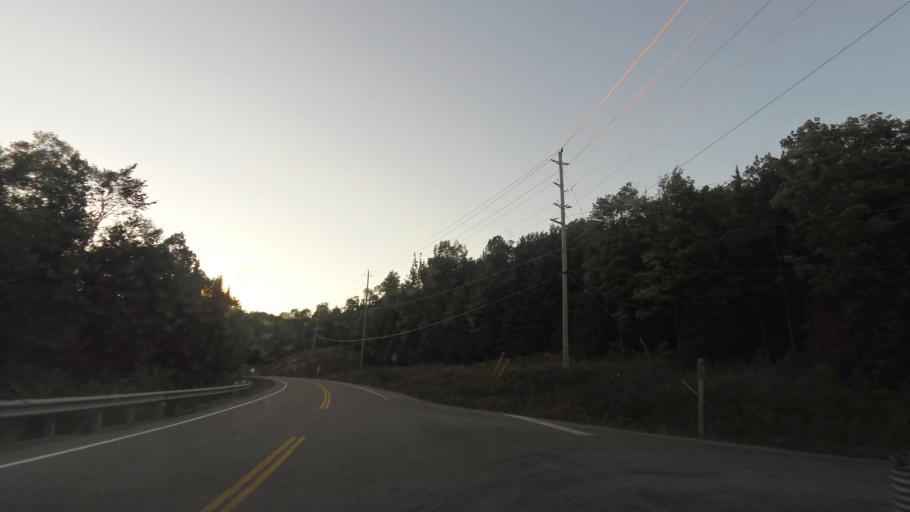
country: CA
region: Ontario
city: Bancroft
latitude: 45.0211
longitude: -78.3533
